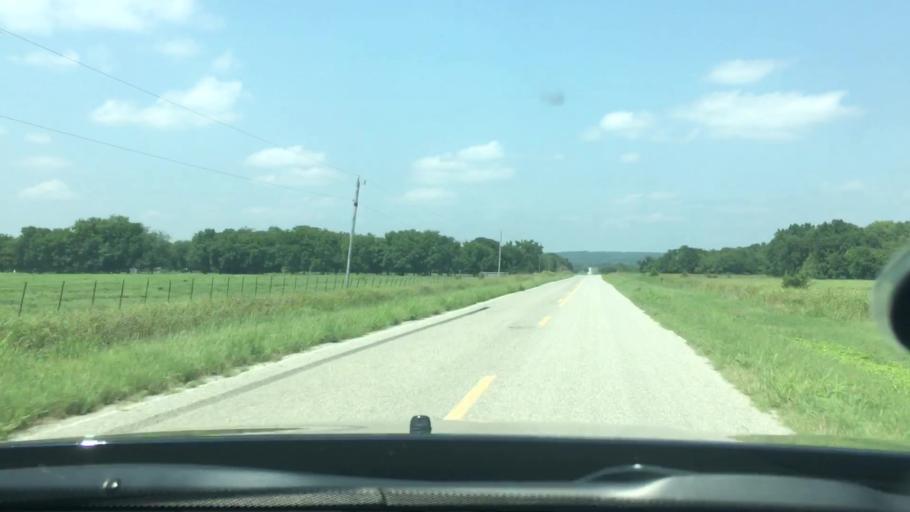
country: US
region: Oklahoma
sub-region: Johnston County
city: Tishomingo
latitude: 34.3830
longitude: -96.4962
